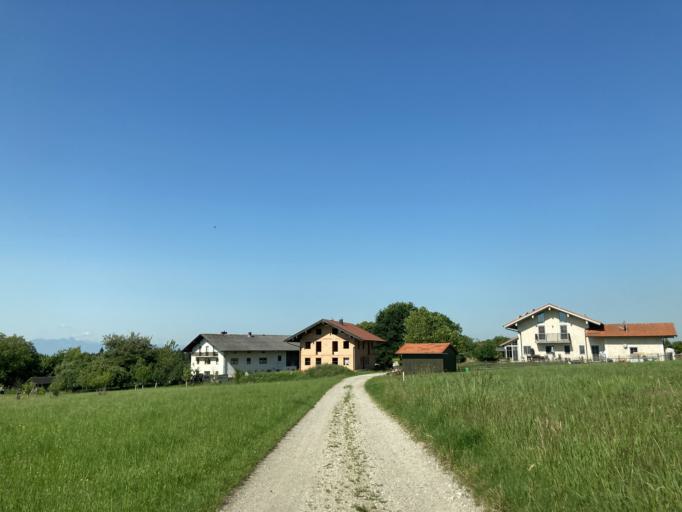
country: DE
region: Bavaria
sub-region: Upper Bavaria
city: Hoslwang
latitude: 47.9663
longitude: 12.3266
